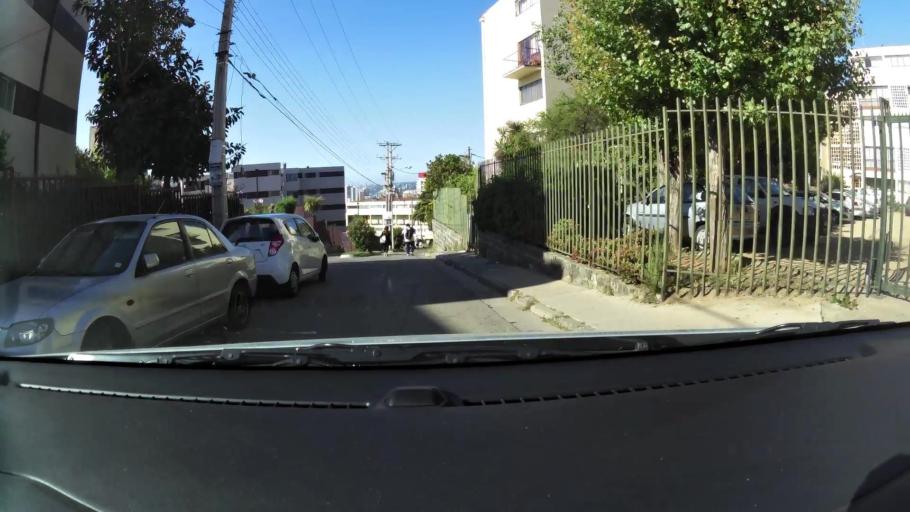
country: CL
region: Valparaiso
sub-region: Provincia de Valparaiso
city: Vina del Mar
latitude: -33.0284
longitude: -71.5567
